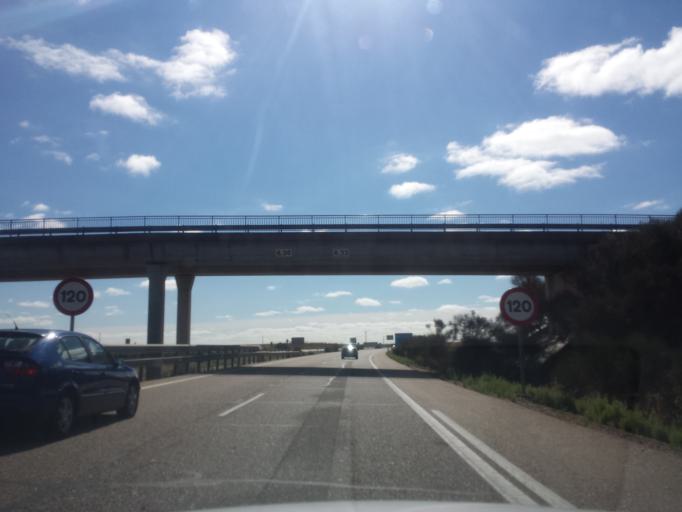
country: ES
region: Castille and Leon
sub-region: Provincia de Zamora
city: Villalpando
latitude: 41.8547
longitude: -5.4154
